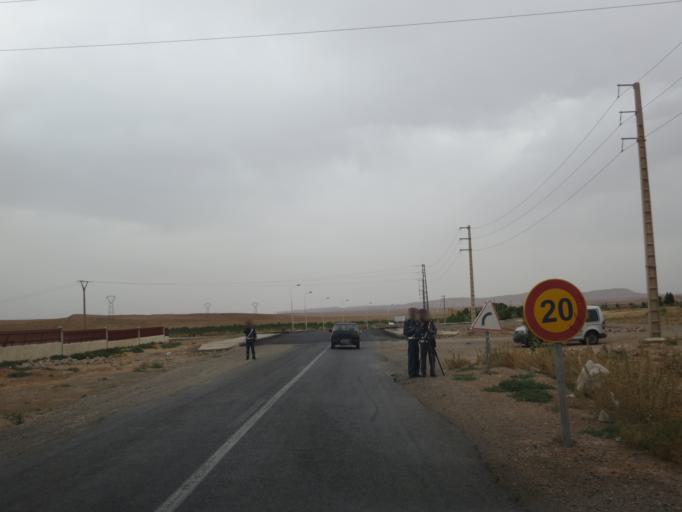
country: MA
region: Meknes-Tafilalet
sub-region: Khenifra
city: Midelt
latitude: 32.7060
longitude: -4.7992
